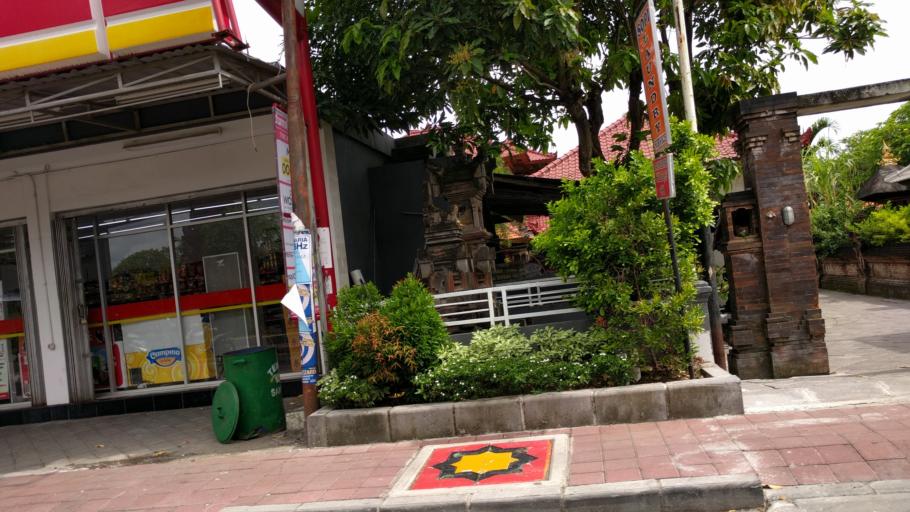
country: ID
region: Bali
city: Kuta
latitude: -8.6730
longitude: 115.1526
